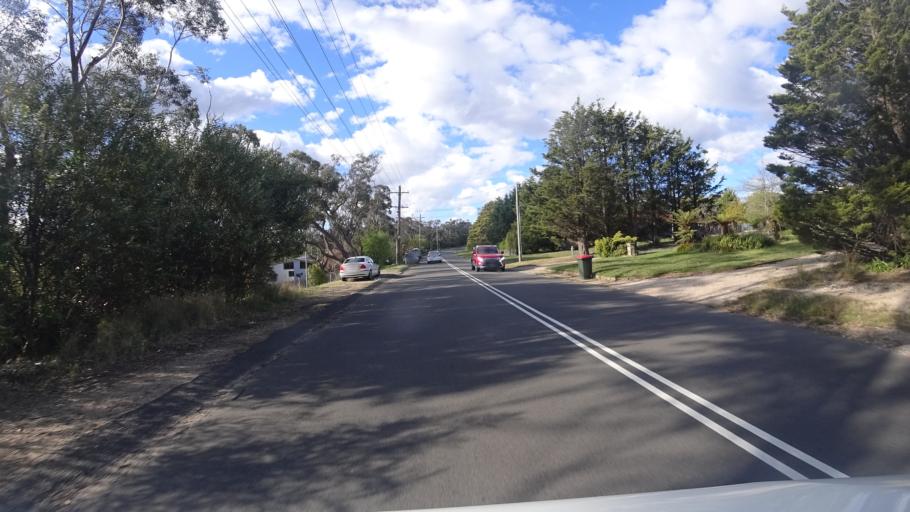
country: AU
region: New South Wales
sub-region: Blue Mountains Municipality
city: Katoomba
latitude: -33.7136
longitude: 150.2979
